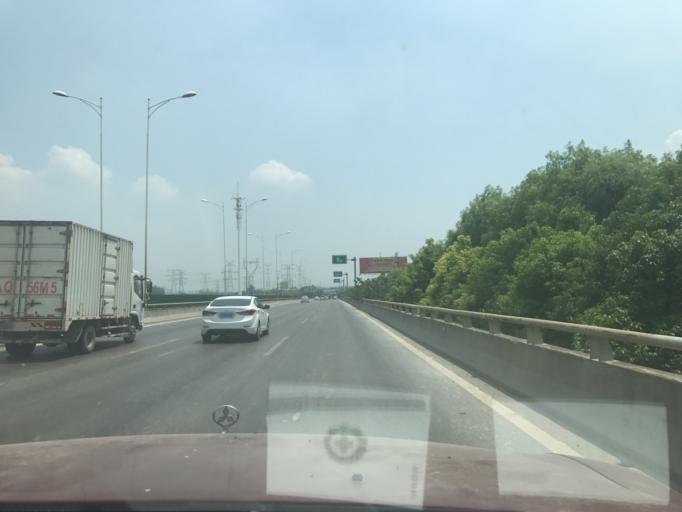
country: CN
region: Hubei
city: Houhu
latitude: 30.6861
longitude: 114.3274
